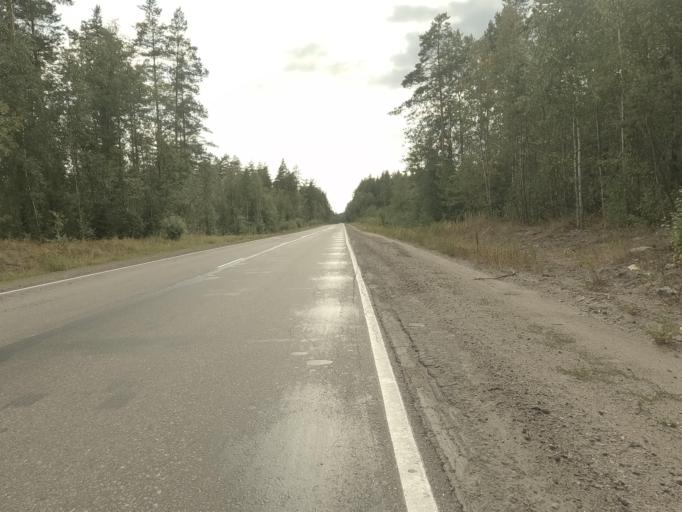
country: RU
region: Leningrad
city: Kamennogorsk
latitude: 60.8804
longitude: 29.0270
